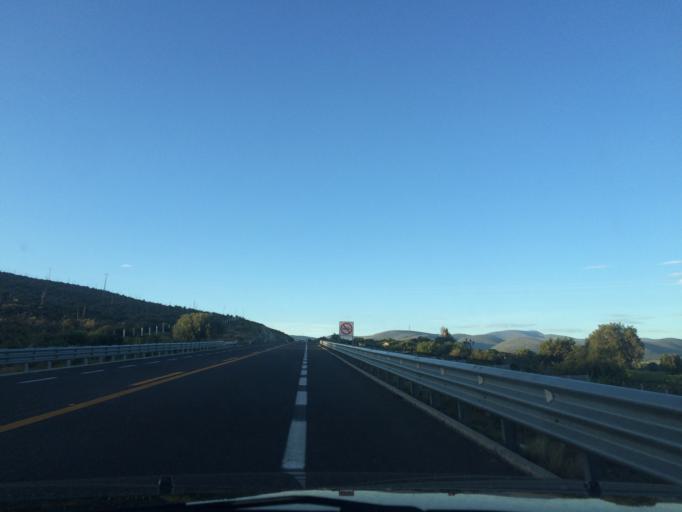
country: MX
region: Puebla
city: Cuacnopalan
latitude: 18.7919
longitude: -97.4891
